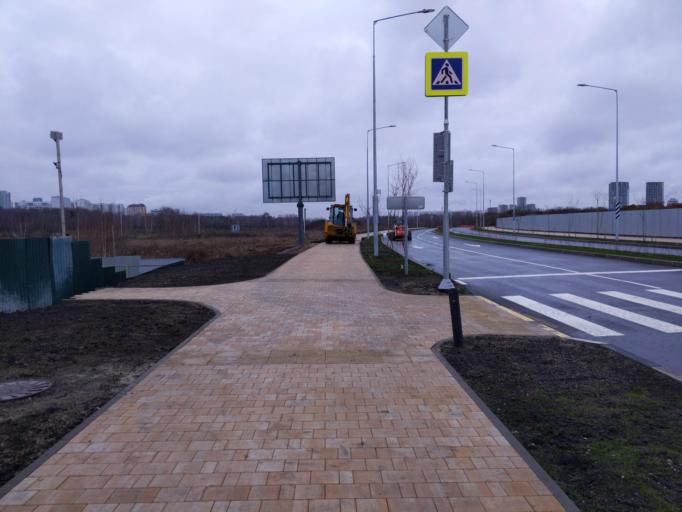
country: RU
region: Moscow
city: Strogino
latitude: 55.8135
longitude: 37.4216
